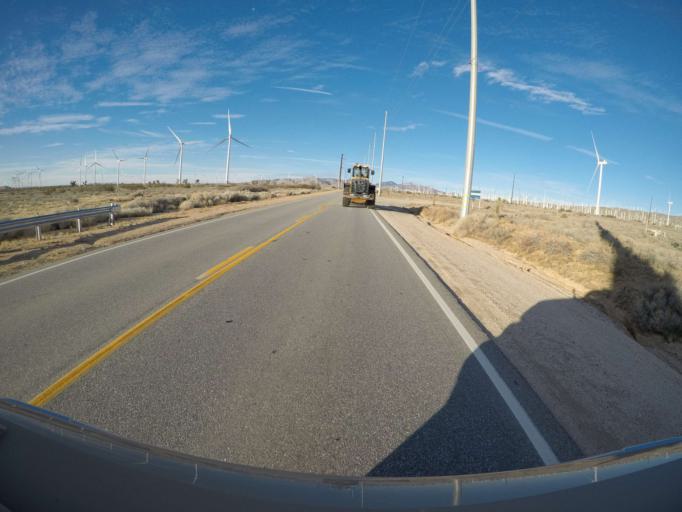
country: US
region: California
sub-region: Kern County
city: Mojave
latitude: 35.0394
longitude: -118.2499
